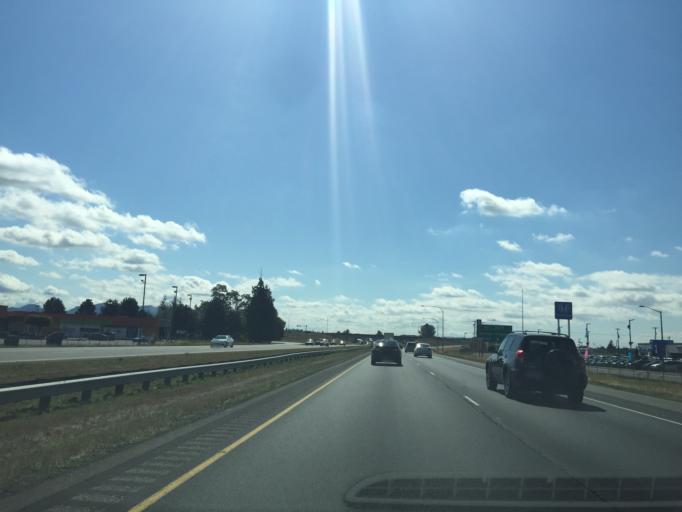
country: US
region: Washington
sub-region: Skagit County
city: Burlington
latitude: 48.4565
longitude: -122.3415
